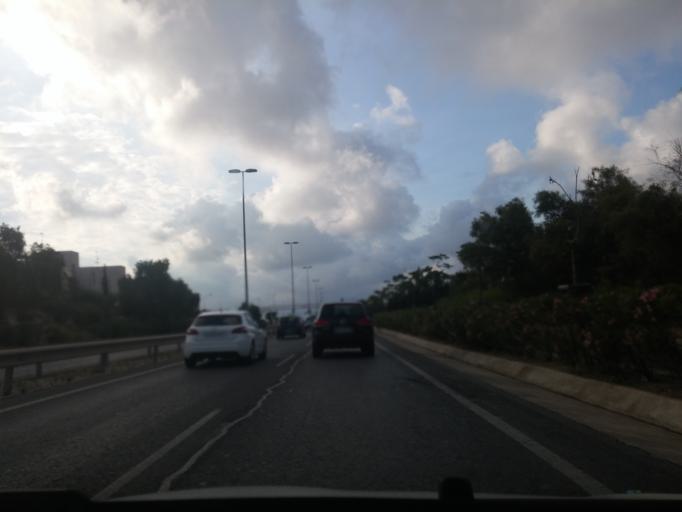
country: ES
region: Valencia
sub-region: Provincia de Alicante
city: Alicante
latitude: 38.3681
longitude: -0.5023
